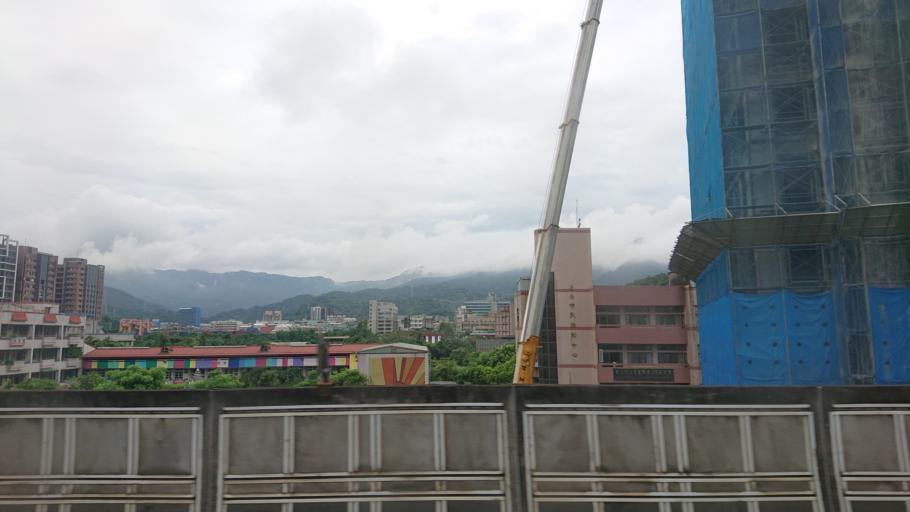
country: TW
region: Taiwan
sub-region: Keelung
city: Keelung
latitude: 25.0797
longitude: 121.6704
